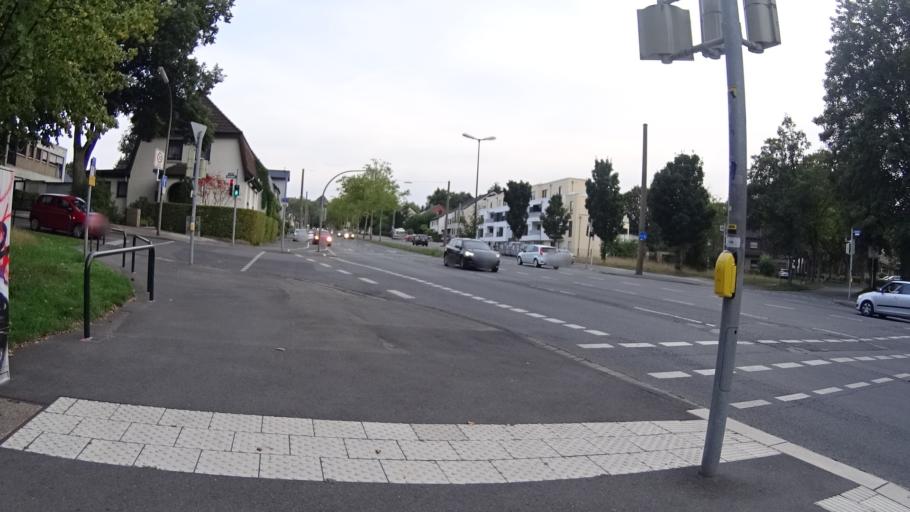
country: DE
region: North Rhine-Westphalia
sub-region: Regierungsbezirk Arnsberg
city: Dortmund
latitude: 51.4856
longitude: 7.4603
